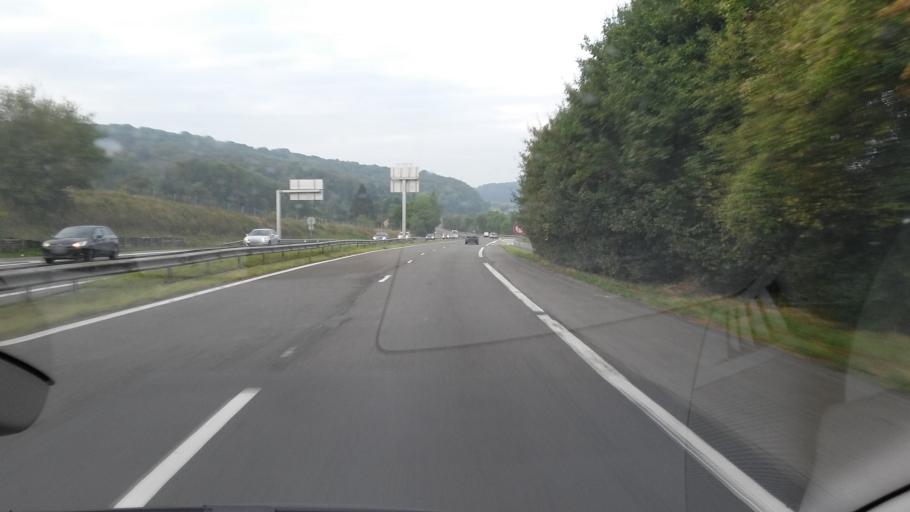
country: FR
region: Champagne-Ardenne
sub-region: Departement des Ardennes
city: La Francheville
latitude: 49.6768
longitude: 4.6585
